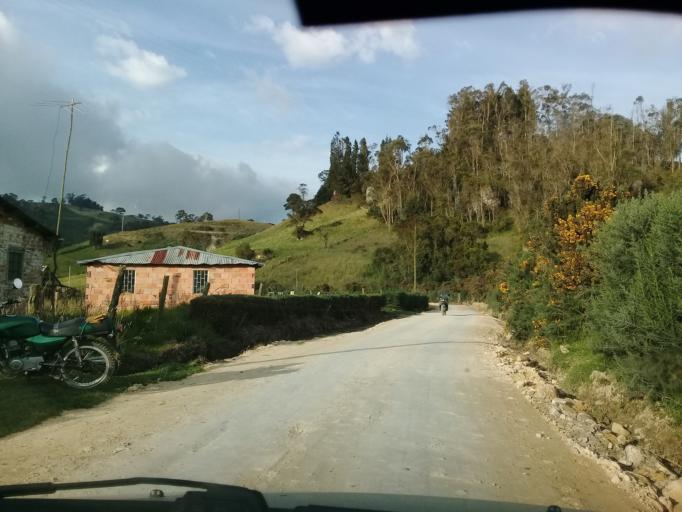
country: CO
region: Cundinamarca
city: Sibate
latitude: 4.4313
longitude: -74.2869
